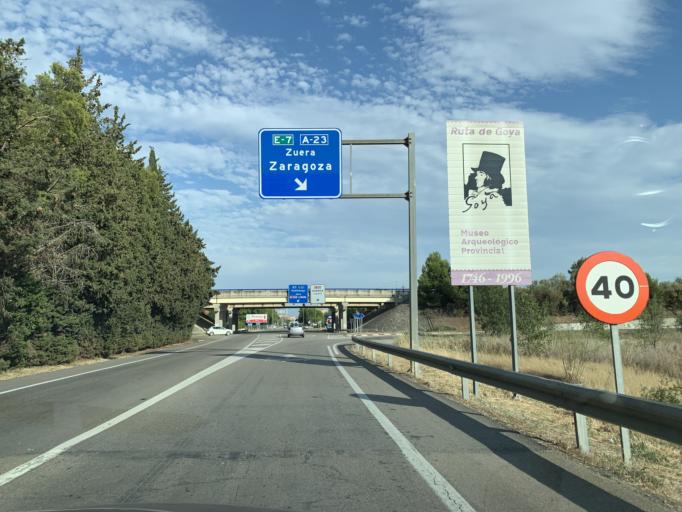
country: ES
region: Aragon
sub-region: Provincia de Huesca
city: Huesca
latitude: 42.1495
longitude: -0.4277
